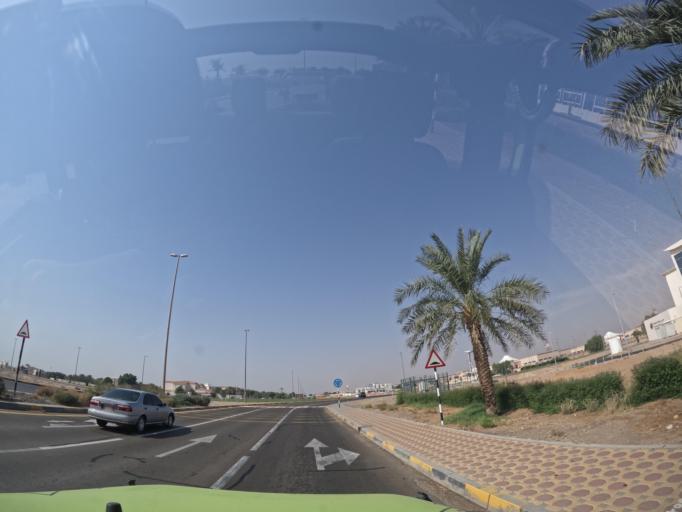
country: AE
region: Abu Dhabi
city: Al Ain
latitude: 24.2569
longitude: 55.6930
